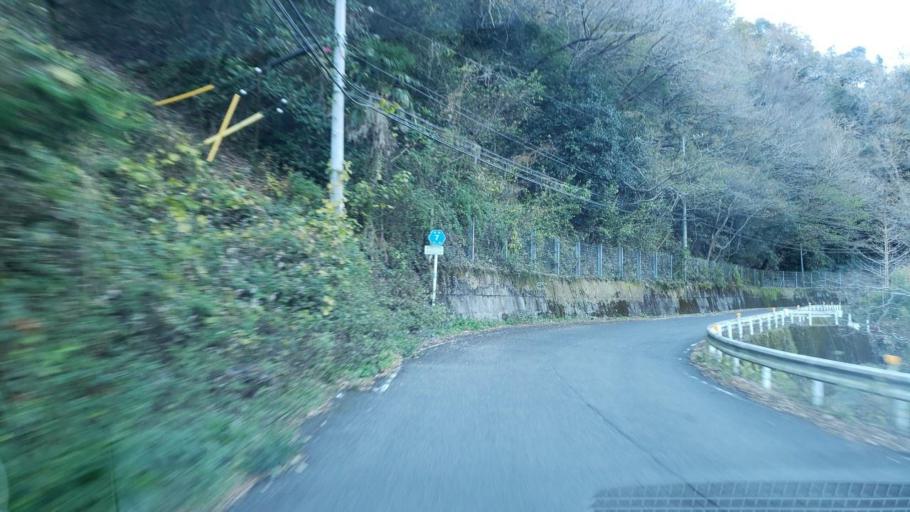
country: JP
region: Tokushima
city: Wakimachi
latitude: 34.0816
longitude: 134.0722
